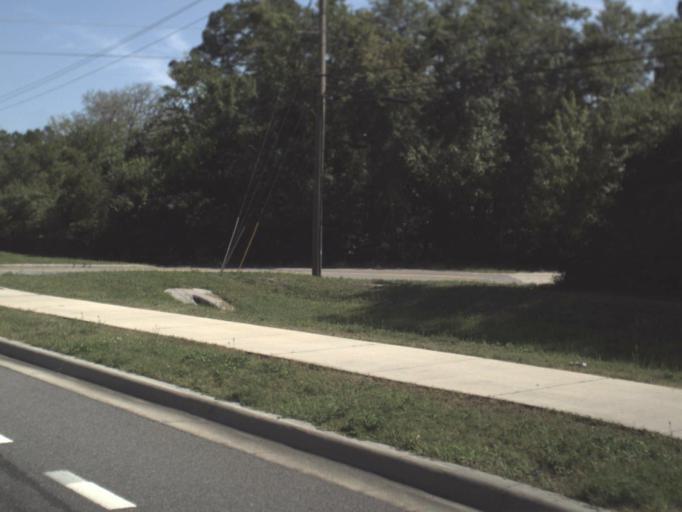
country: US
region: Florida
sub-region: Clay County
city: Green Cove Springs
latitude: 29.9683
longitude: -81.4995
